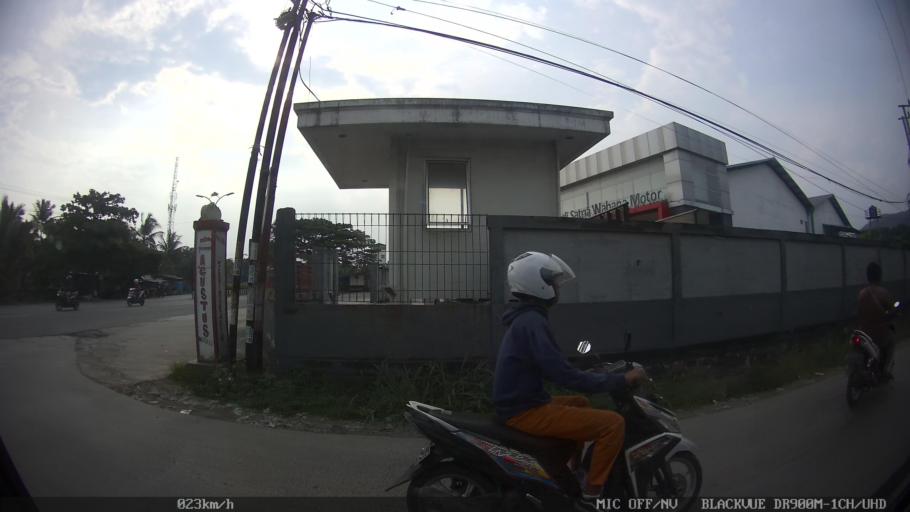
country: ID
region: Lampung
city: Panjang
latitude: -5.4476
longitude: 105.3024
